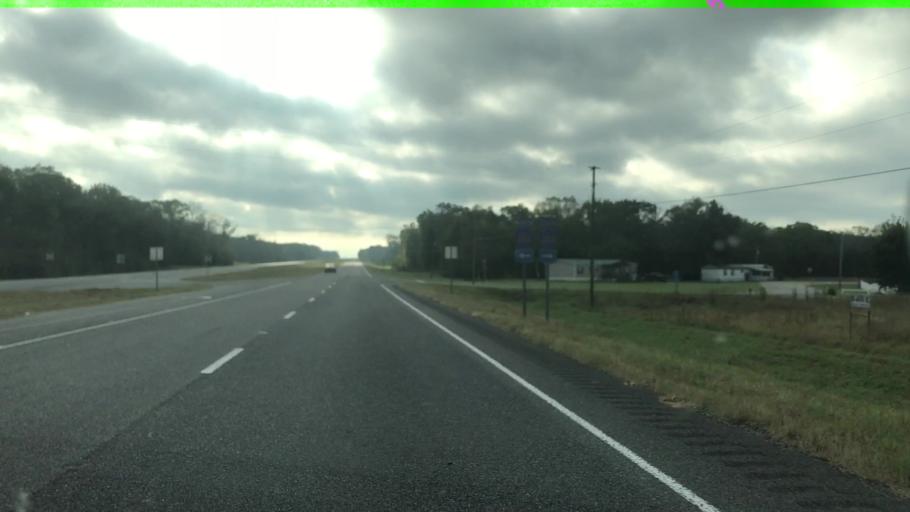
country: US
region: Alabama
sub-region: Morgan County
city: Danville
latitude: 34.4103
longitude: -87.1500
